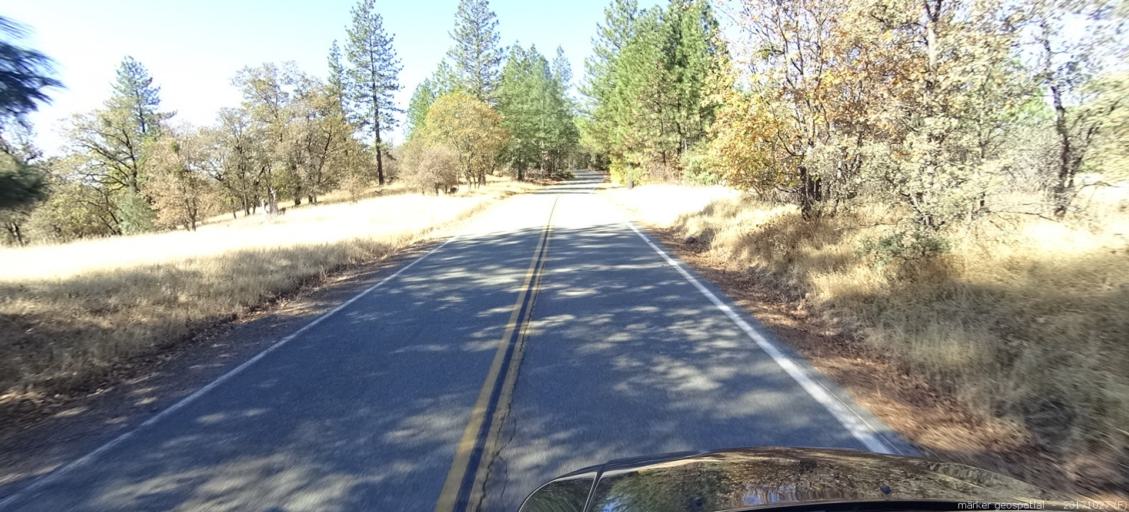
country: US
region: California
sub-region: Shasta County
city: Bella Vista
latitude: 40.7527
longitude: -121.9816
